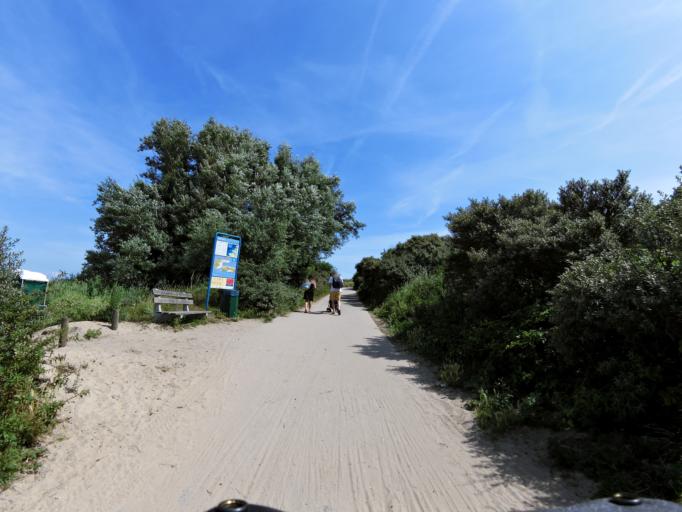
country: NL
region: Zeeland
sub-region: Schouwen-Duiveland
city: Burgh
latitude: 51.6680
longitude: 3.7126
